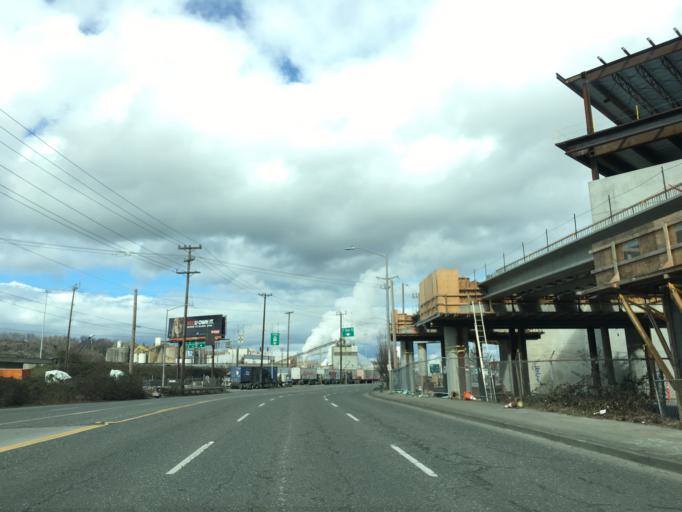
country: US
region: Washington
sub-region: King County
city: White Center
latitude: 47.5453
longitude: -122.3319
